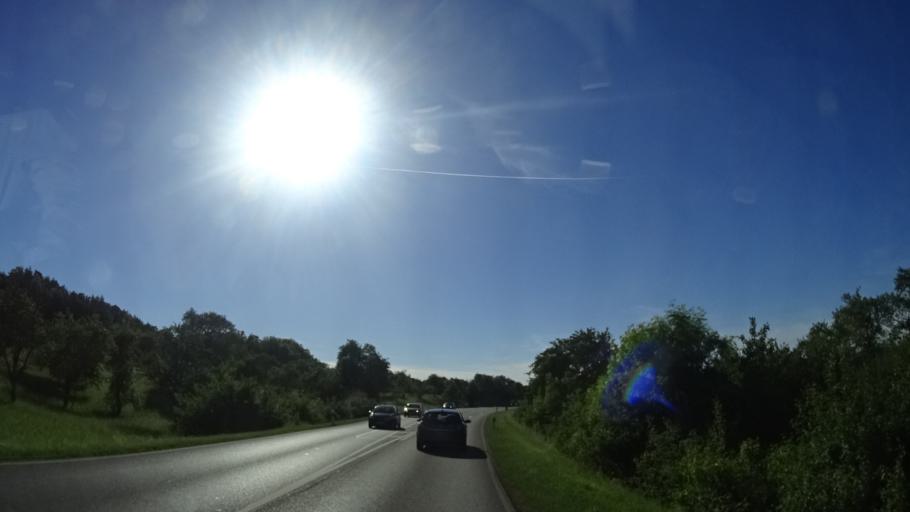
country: DE
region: Baden-Wuerttemberg
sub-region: Regierungsbezirk Stuttgart
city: Vellberg
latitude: 49.0920
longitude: 9.8414
